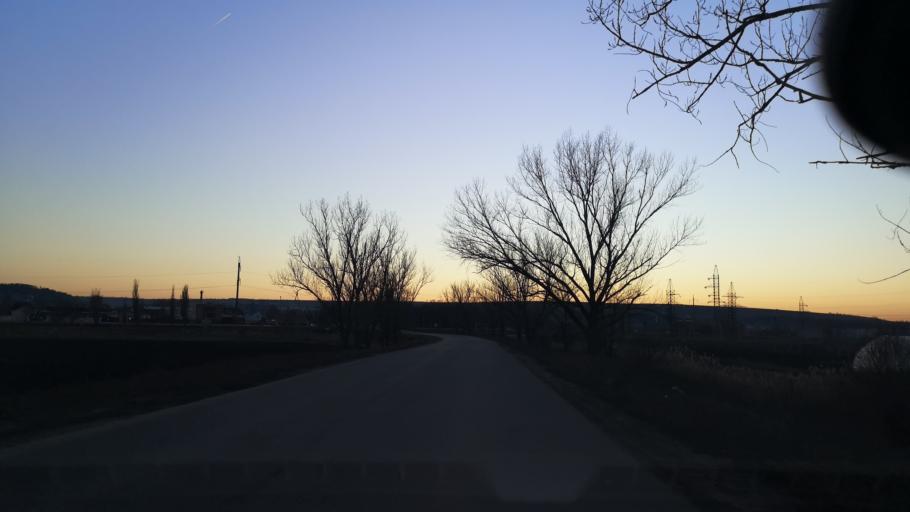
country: MD
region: Anenii Noi
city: Anenii Noi
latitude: 46.8882
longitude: 29.2378
